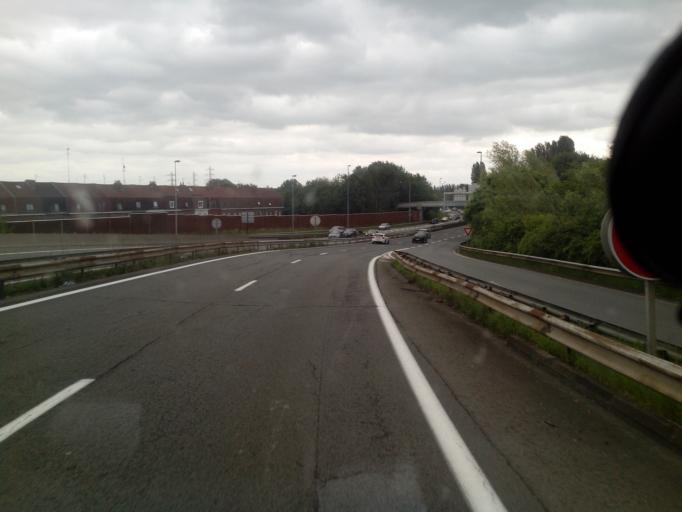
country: FR
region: Nord-Pas-de-Calais
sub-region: Departement du Nord
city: Wasquehal
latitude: 50.6488
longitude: 3.1488
